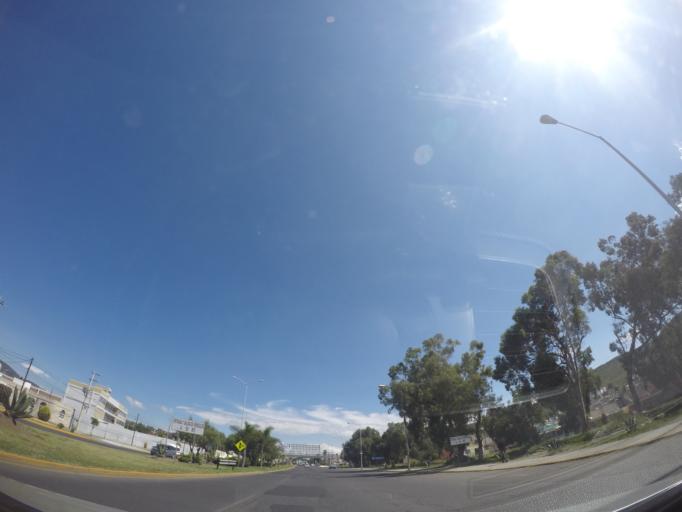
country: MX
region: Hidalgo
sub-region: Mineral de la Reforma
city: Unidad Minera 11 de Julio
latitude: 20.1087
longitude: -98.7217
